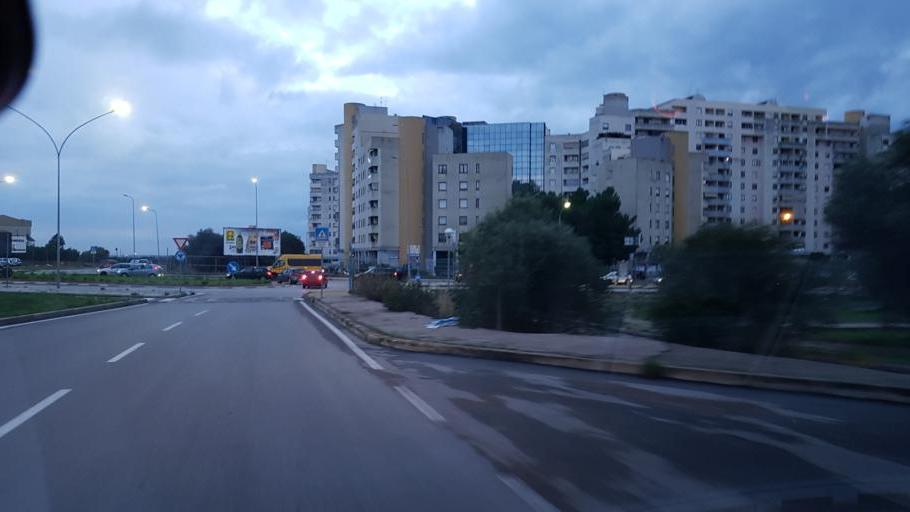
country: IT
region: Apulia
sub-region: Provincia di Taranto
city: Paolo VI
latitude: 40.5200
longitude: 17.2812
